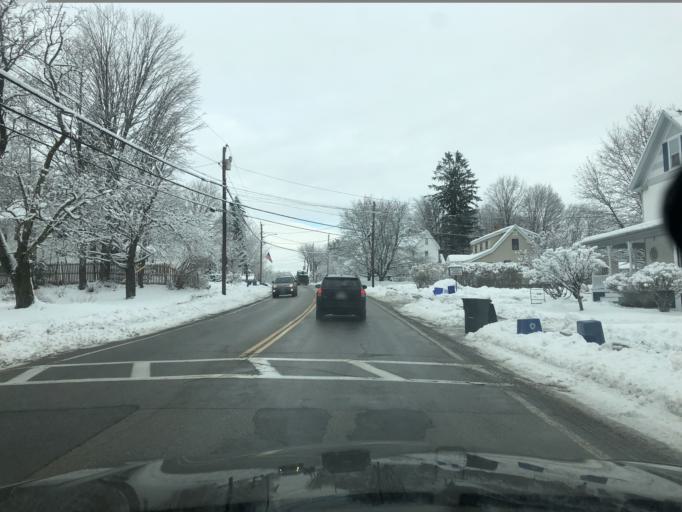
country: US
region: New Hampshire
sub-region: Strafford County
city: Somersworth
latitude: 43.2503
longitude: -70.8720
